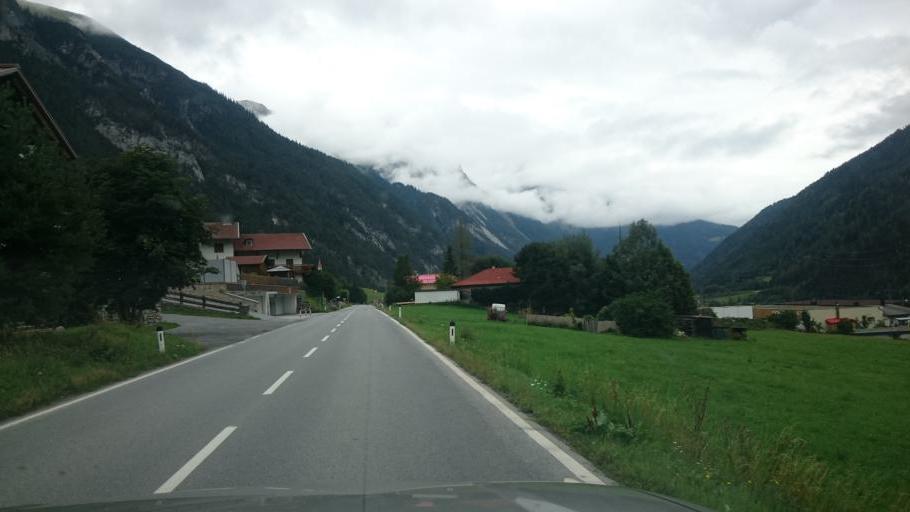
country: AT
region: Tyrol
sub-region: Politischer Bezirk Landeck
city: Flirsch
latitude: 47.1484
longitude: 10.3440
